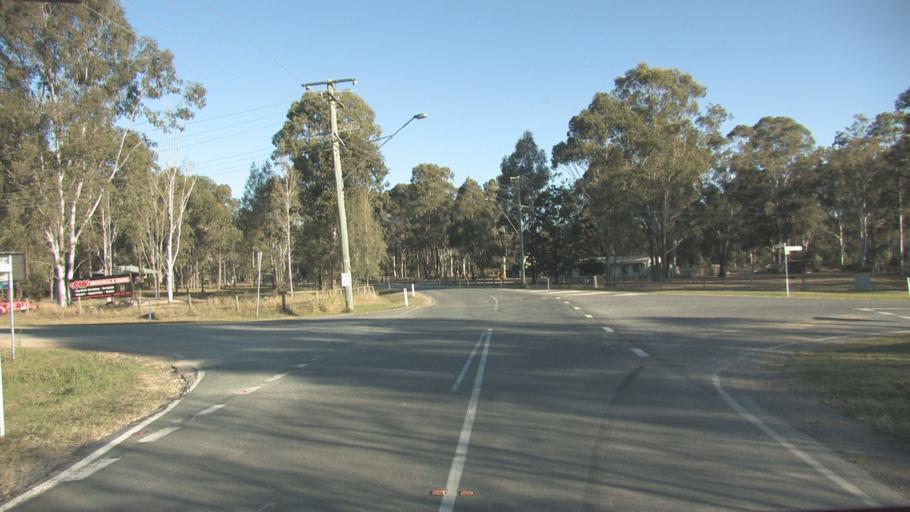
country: AU
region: Queensland
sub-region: Logan
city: Chambers Flat
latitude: -27.7832
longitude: 153.1350
